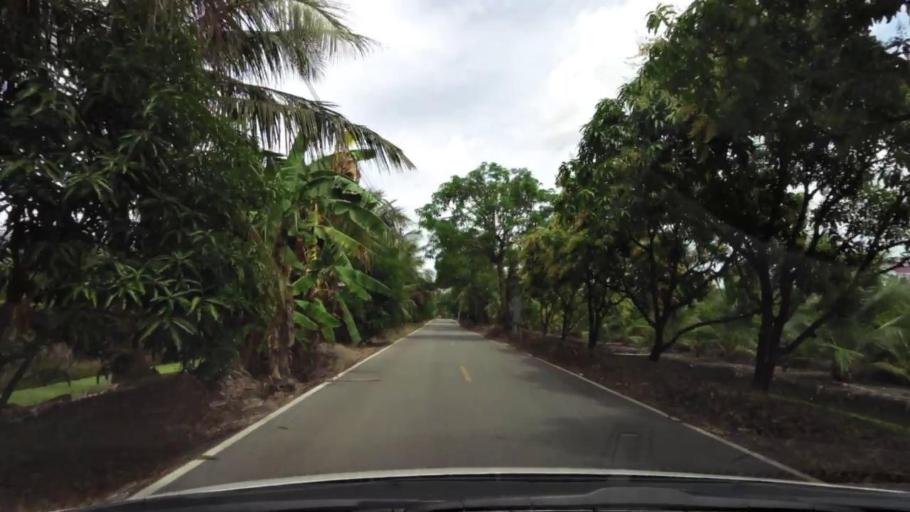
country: TH
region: Ratchaburi
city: Damnoen Saduak
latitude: 13.5126
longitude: 100.0107
